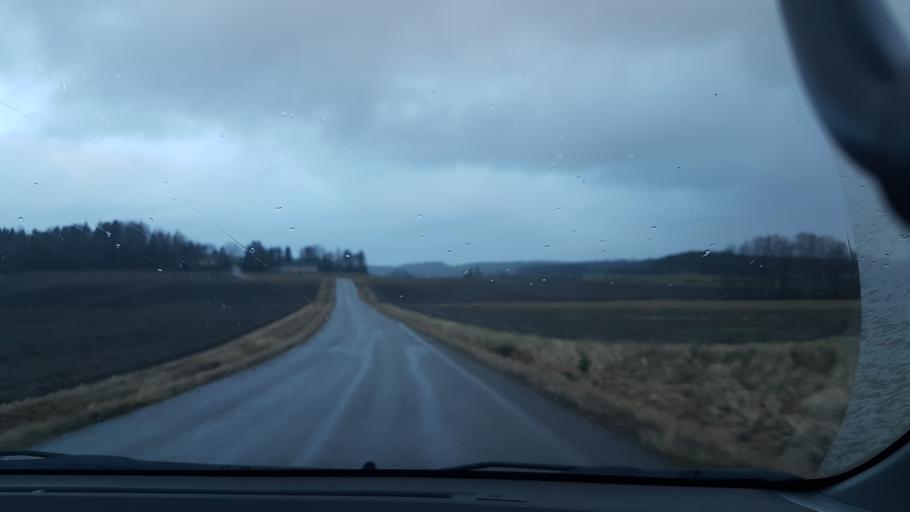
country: FI
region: Uusimaa
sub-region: Helsinki
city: Lohja
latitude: 60.2066
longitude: 24.0994
